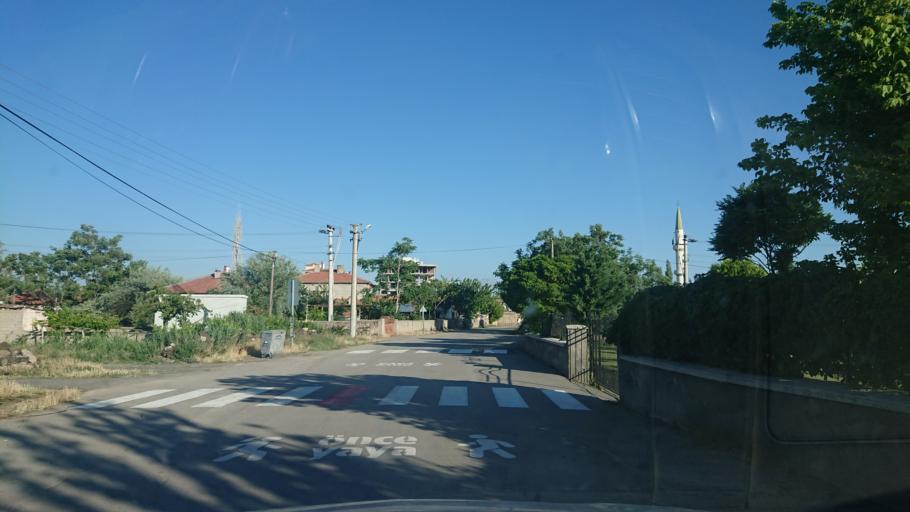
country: TR
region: Aksaray
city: Aksaray
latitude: 38.3849
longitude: 33.9903
